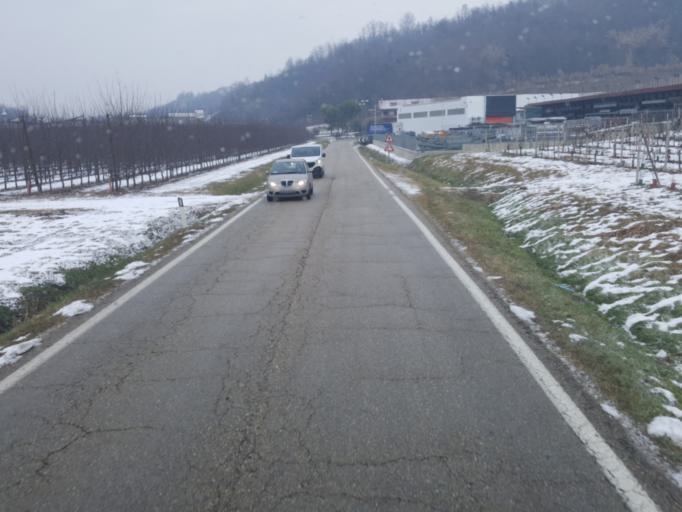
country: IT
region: Piedmont
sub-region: Provincia di Cuneo
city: Vezza d'Alba
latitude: 44.7661
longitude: 8.0200
